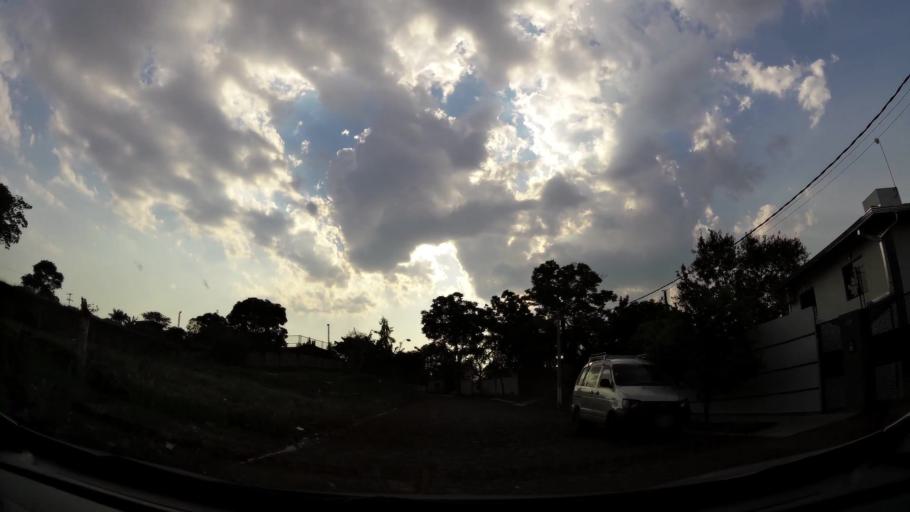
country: PY
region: Alto Parana
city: Ciudad del Este
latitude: -25.5177
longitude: -54.6276
